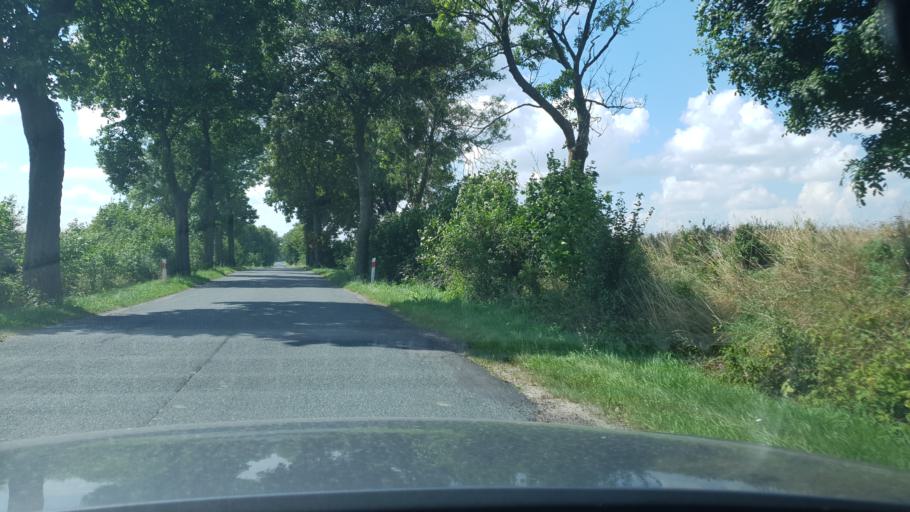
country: PL
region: Kujawsko-Pomorskie
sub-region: Powiat wabrzeski
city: Pluznica
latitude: 53.3769
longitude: 18.8251
